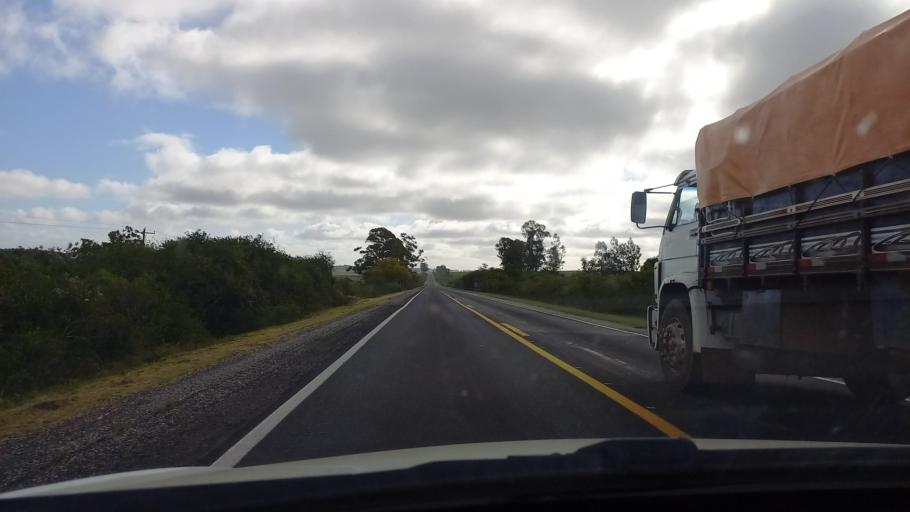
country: BR
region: Rio Grande do Sul
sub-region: Dom Pedrito
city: Dom Pedrito
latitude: -30.8987
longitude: -54.8407
